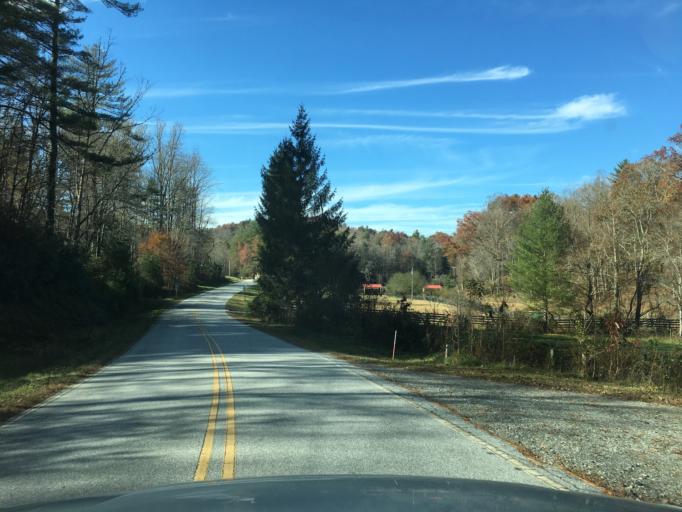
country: US
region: North Carolina
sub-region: Henderson County
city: Etowah
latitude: 35.2242
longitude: -82.5910
